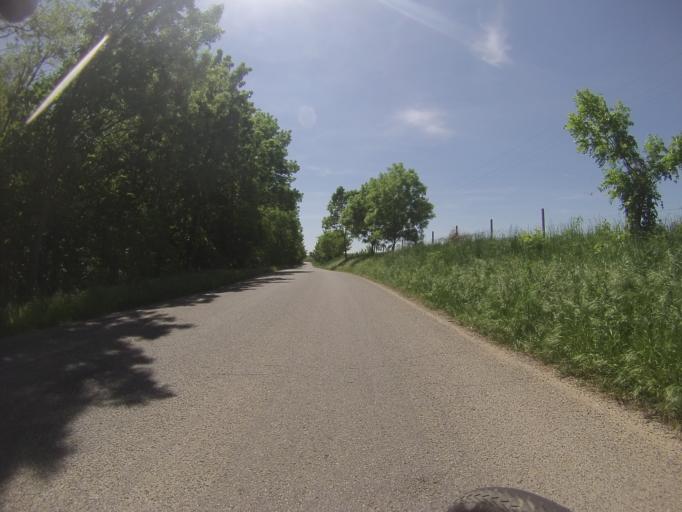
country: CZ
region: South Moravian
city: Vranovice
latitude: 48.9446
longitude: 16.5866
